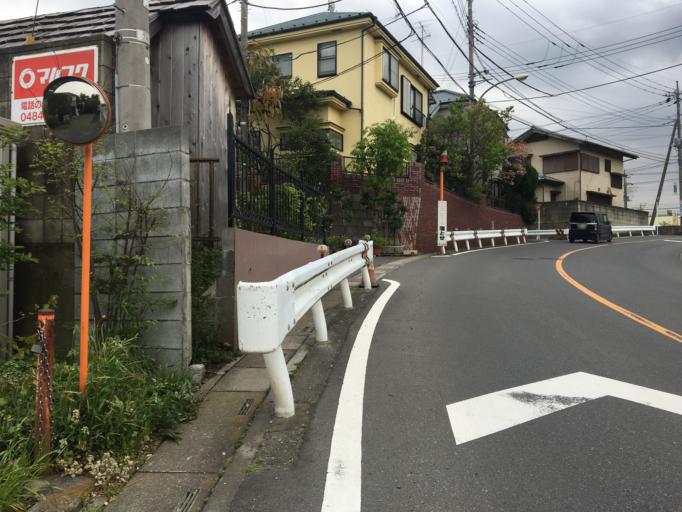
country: JP
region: Saitama
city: Shiki
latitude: 35.8451
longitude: 139.5536
